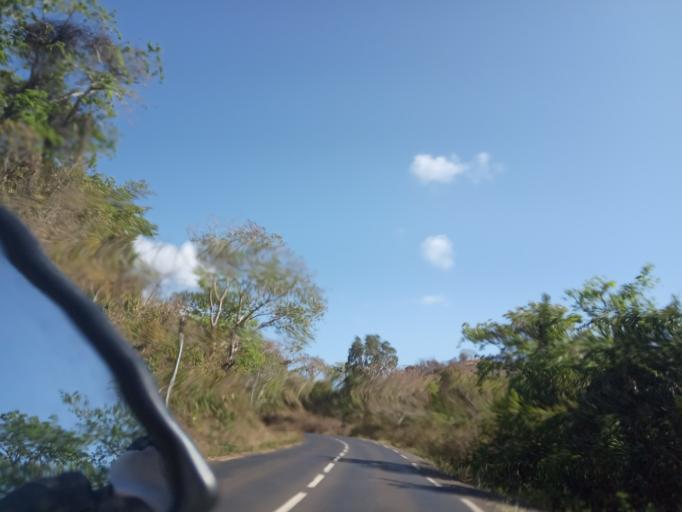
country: YT
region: Dembeni
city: Dembeni
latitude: -12.8699
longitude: 45.2071
